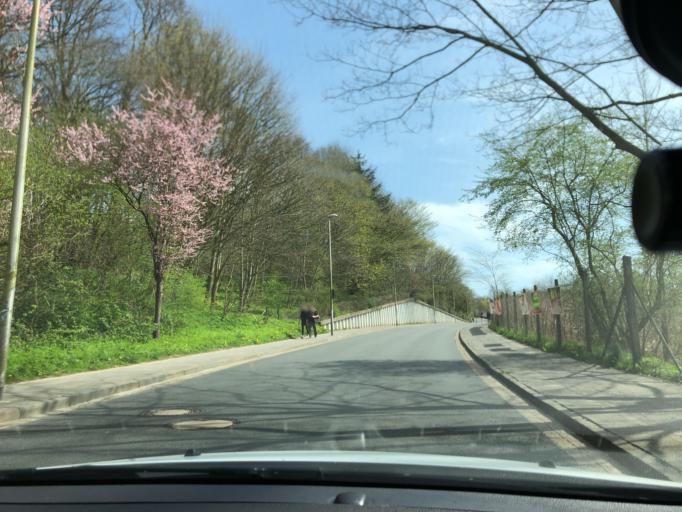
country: DE
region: Schleswig-Holstein
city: Flensburg
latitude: 54.7770
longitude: 9.4430
